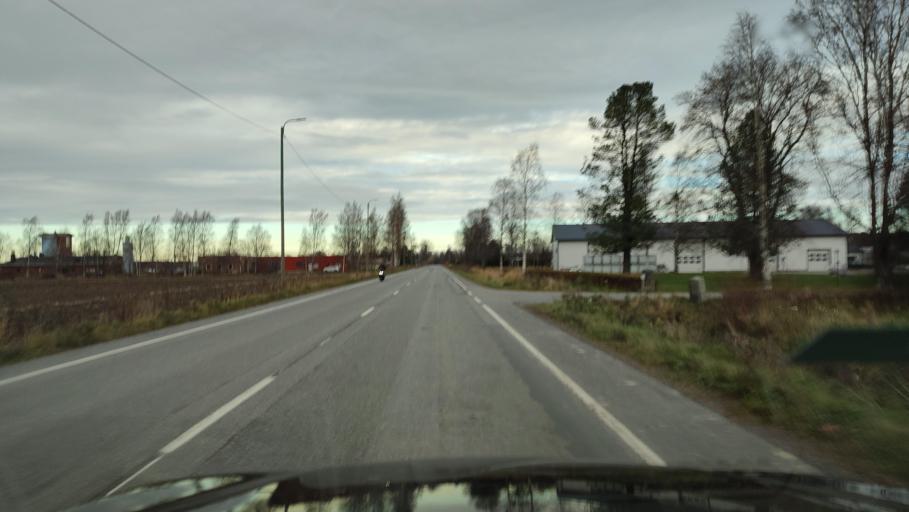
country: FI
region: Ostrobothnia
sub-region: Sydosterbotten
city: Naerpes
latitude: 62.4563
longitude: 21.3543
